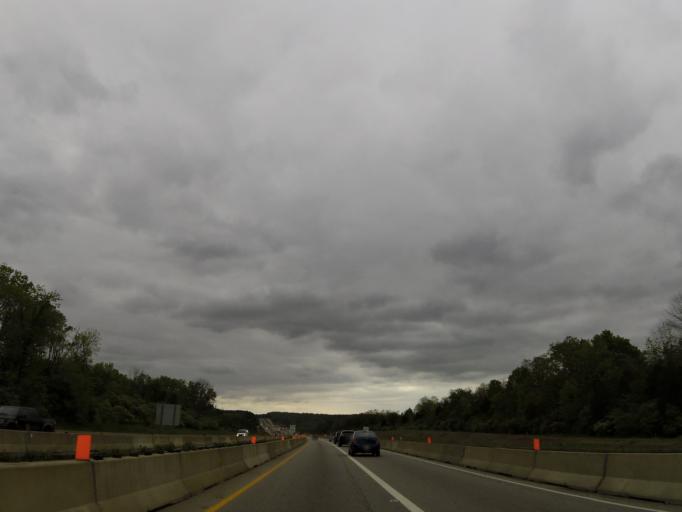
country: US
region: Ohio
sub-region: Warren County
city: Morrow
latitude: 39.4160
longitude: -84.1155
